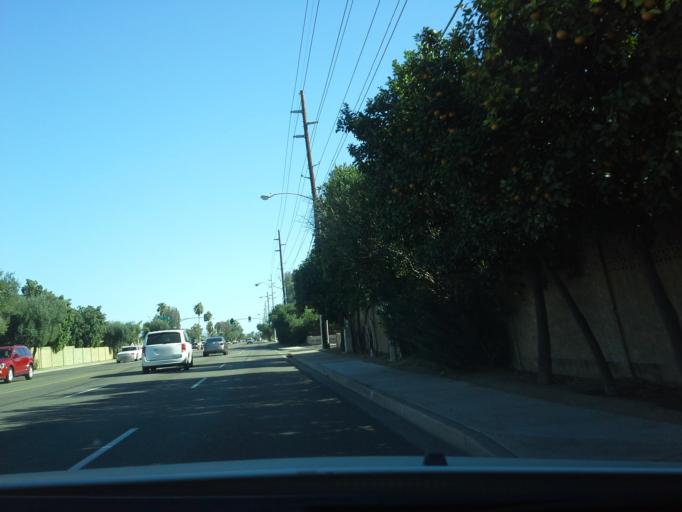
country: US
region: Arizona
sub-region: Maricopa County
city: Paradise Valley
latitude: 33.5825
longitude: -112.0062
